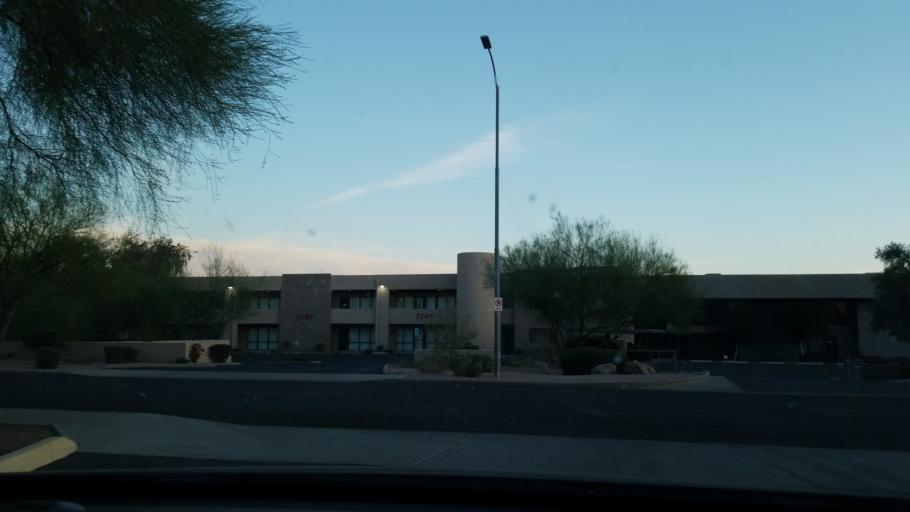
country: US
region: Arizona
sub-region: Maricopa County
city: Paradise Valley
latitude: 33.6258
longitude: -111.9140
